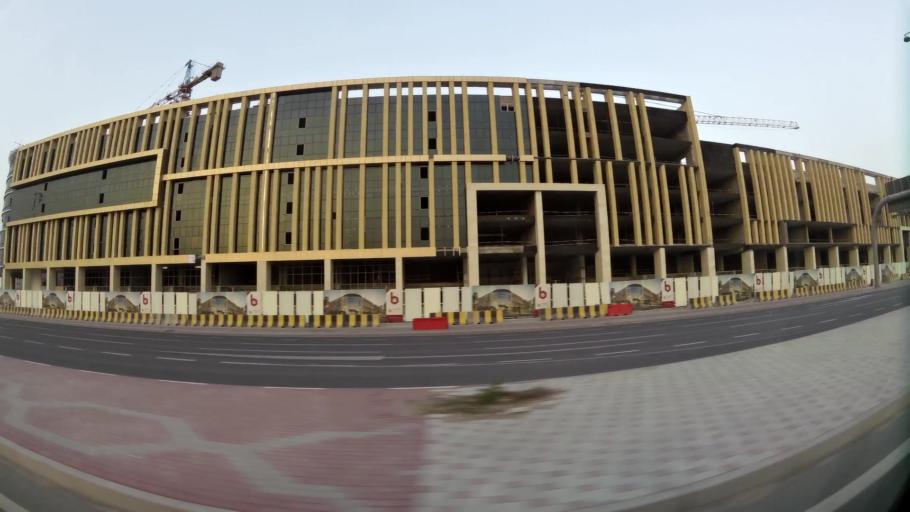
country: QA
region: Baladiyat ad Dawhah
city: Doha
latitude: 25.2522
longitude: 51.4703
